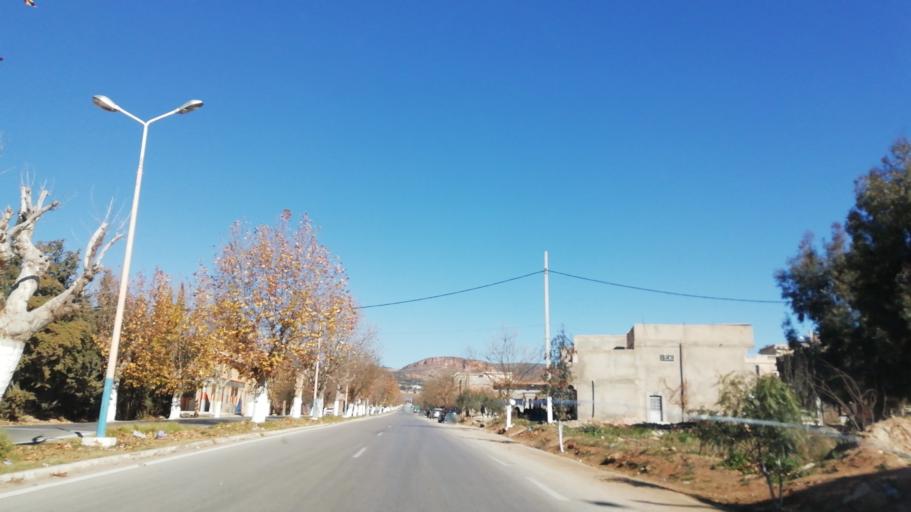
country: DZ
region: Tlemcen
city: Sebdou
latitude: 34.6648
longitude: -1.3213
